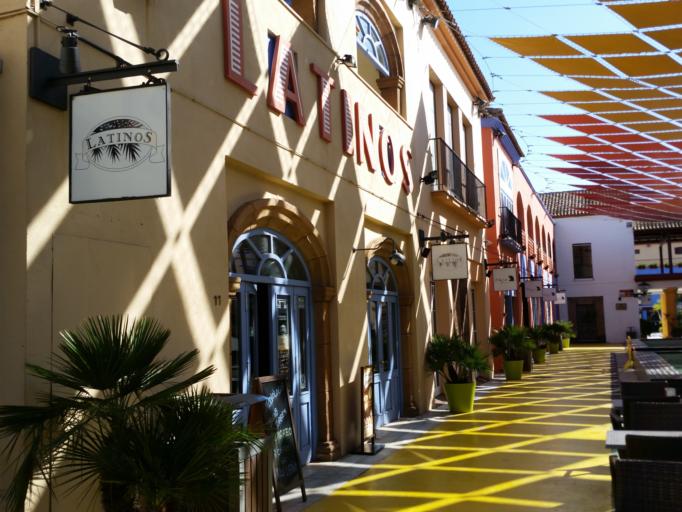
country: ES
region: Andalusia
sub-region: Provincia de Malaga
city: Torremolinos
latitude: 36.6580
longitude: -4.4784
